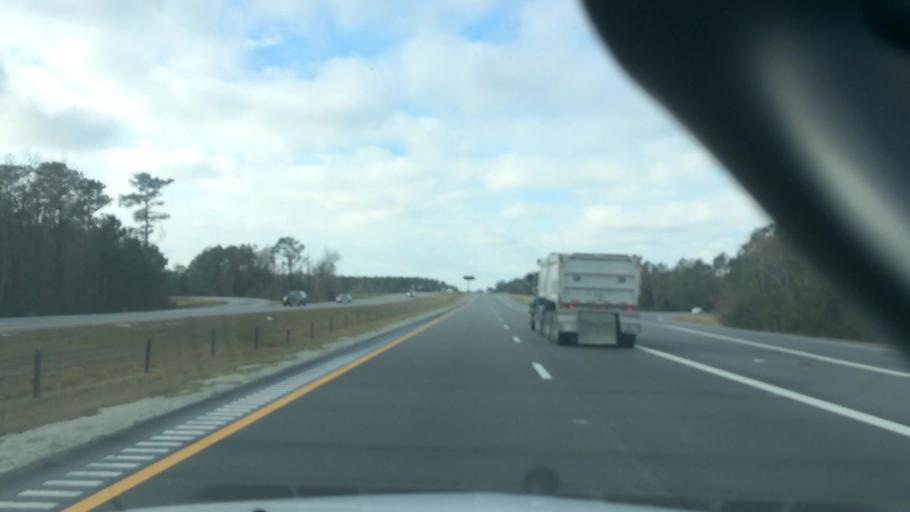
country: US
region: North Carolina
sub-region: New Hanover County
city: Wrightsboro
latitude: 34.3161
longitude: -77.9168
